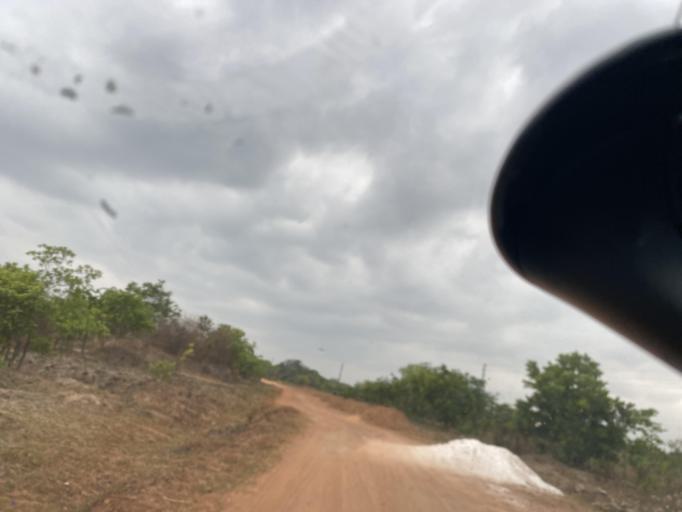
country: ZM
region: Lusaka
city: Chongwe
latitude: -15.2332
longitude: 28.7222
